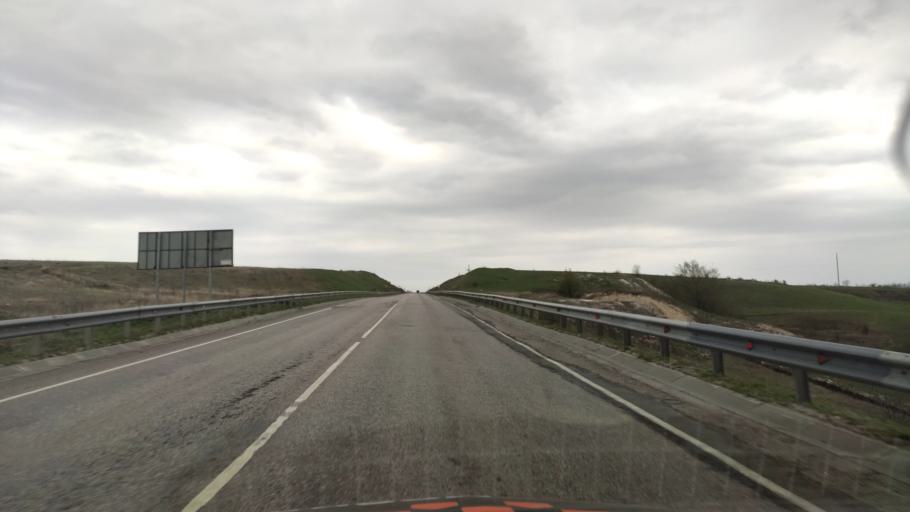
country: RU
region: Voronezj
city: Nizhnedevitsk
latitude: 51.5645
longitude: 38.3718
